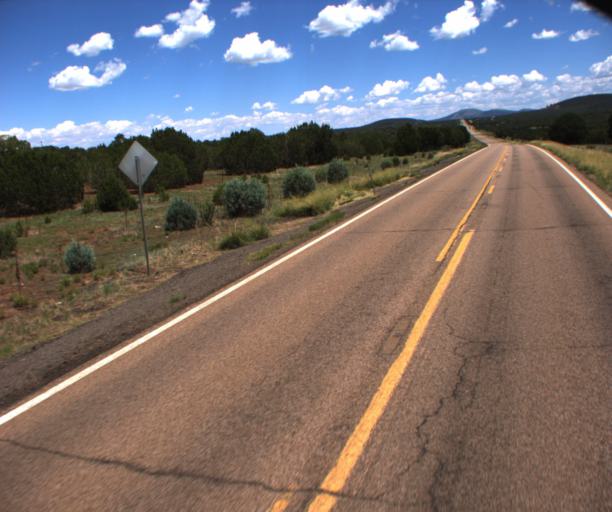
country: US
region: Arizona
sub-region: Navajo County
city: Pinetop-Lakeside
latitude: 34.2770
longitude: -109.7926
